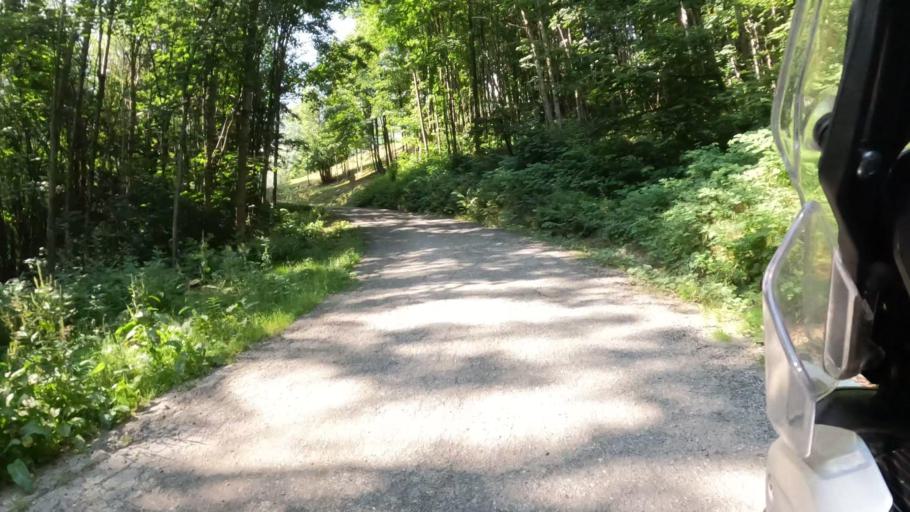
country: IT
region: Piedmont
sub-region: Provincia di Torino
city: Lemie
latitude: 45.2145
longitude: 7.3119
